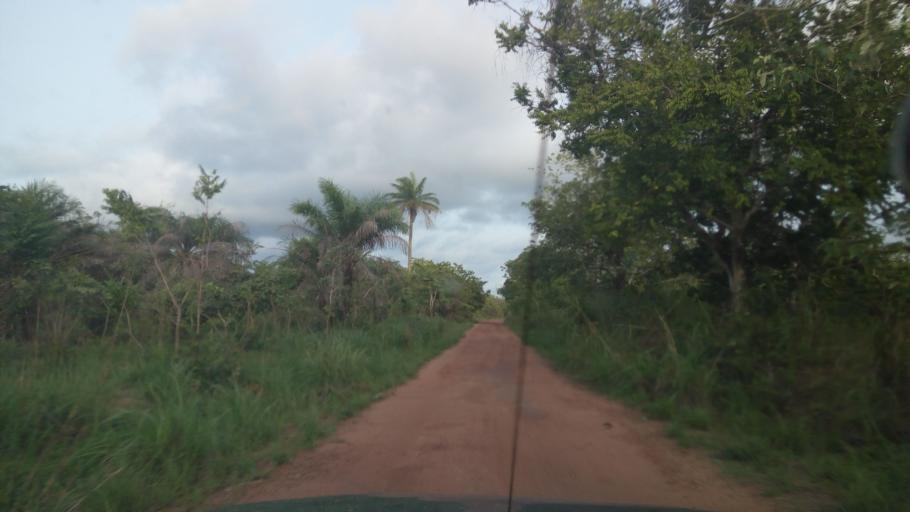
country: SL
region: Northern Province
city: Kassiri
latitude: 9.0334
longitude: -13.0705
